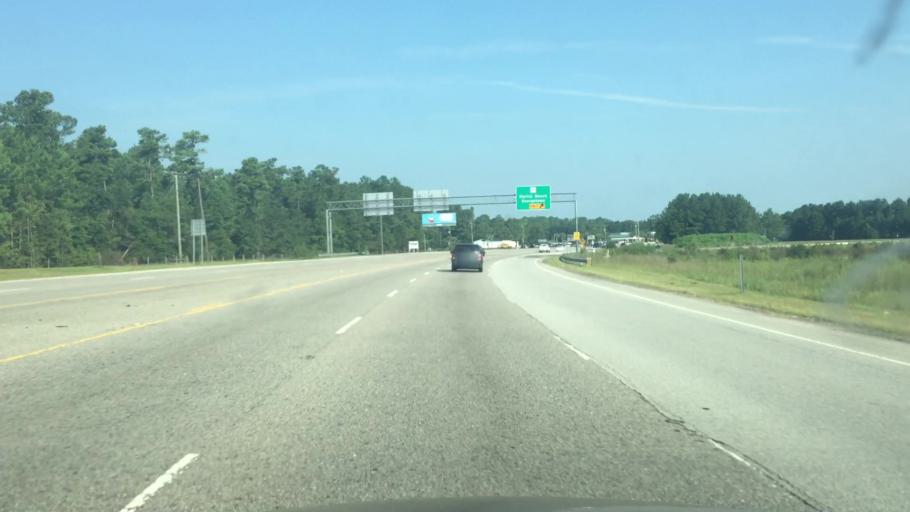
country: US
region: South Carolina
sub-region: Horry County
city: North Myrtle Beach
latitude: 33.8762
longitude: -78.6831
